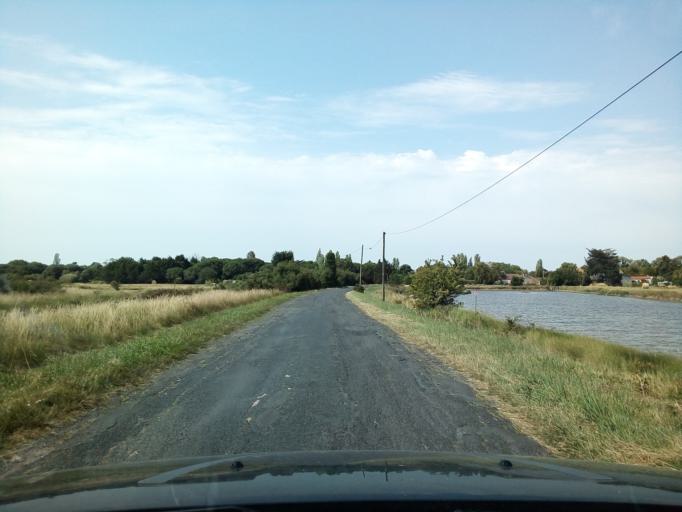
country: FR
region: Poitou-Charentes
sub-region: Departement de la Charente-Maritime
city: Boyard-Ville
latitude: 45.9588
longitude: -1.2554
